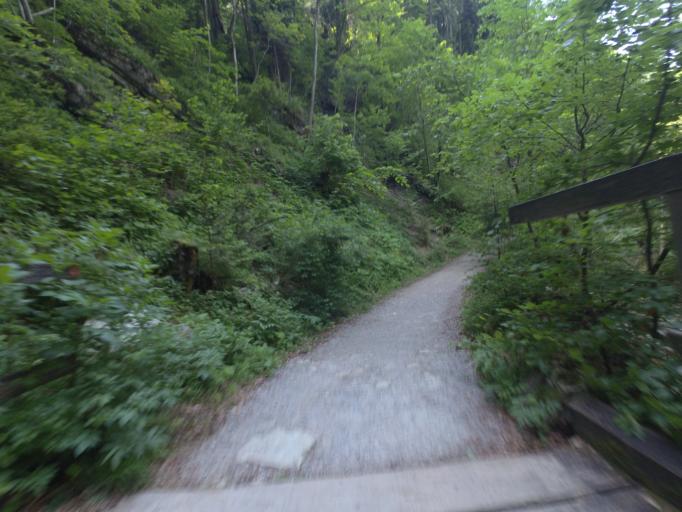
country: AT
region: Salzburg
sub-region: Politischer Bezirk Salzburg-Umgebung
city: Elsbethen
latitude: 47.7691
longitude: 13.1162
